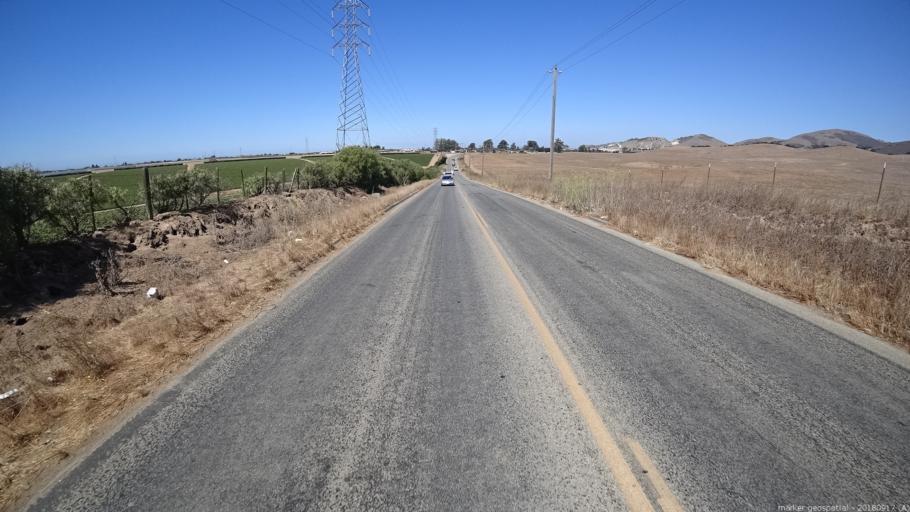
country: US
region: California
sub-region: Monterey County
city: Salinas
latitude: 36.7163
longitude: -121.5907
